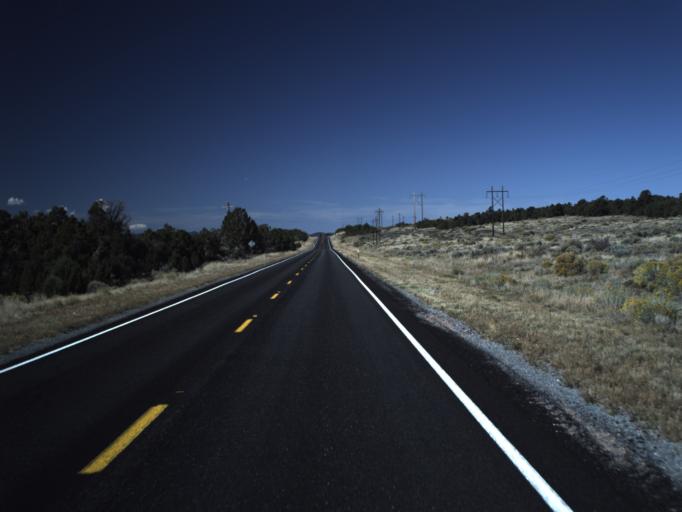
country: US
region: Utah
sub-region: Iron County
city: Cedar City
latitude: 37.6109
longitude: -113.3758
